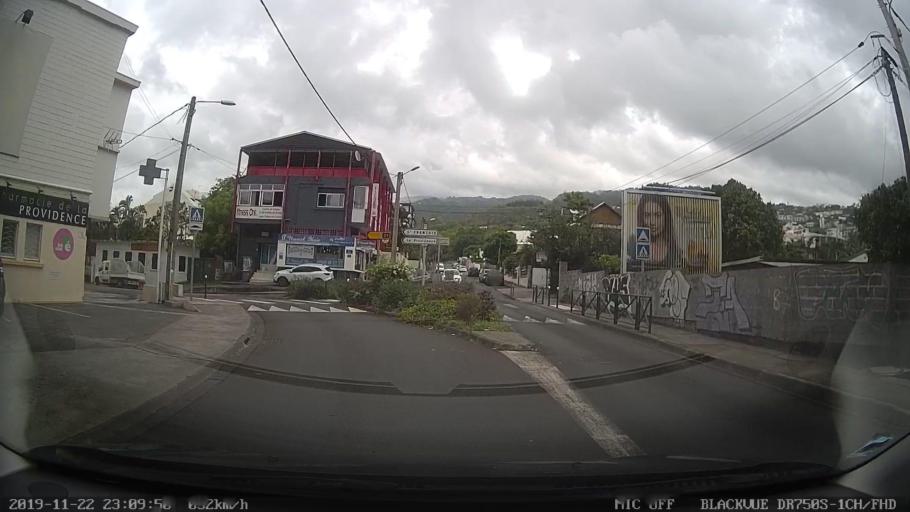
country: RE
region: Reunion
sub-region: Reunion
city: Saint-Denis
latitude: -20.8905
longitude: 55.4528
